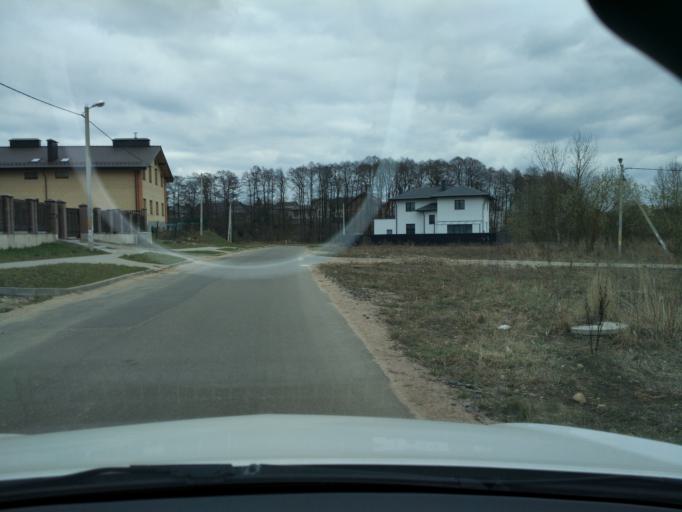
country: BY
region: Minsk
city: Bal'shavik
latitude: 53.9669
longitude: 27.5852
